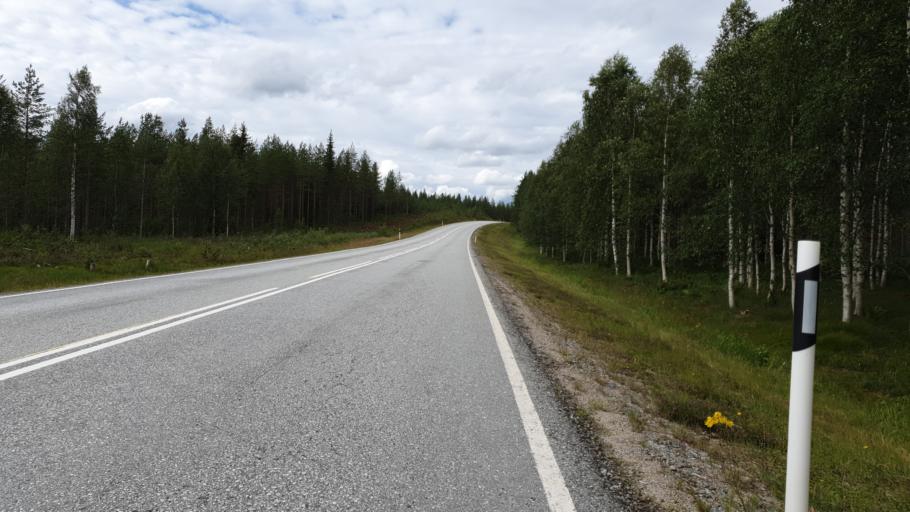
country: FI
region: Kainuu
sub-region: Kehys-Kainuu
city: Kuhmo
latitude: 64.4807
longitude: 29.7702
